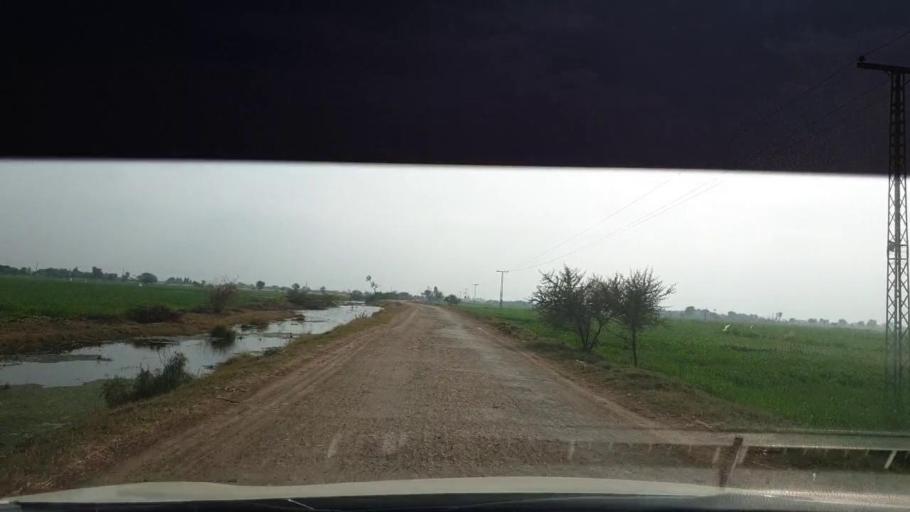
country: PK
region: Sindh
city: Berani
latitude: 25.7729
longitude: 68.8758
